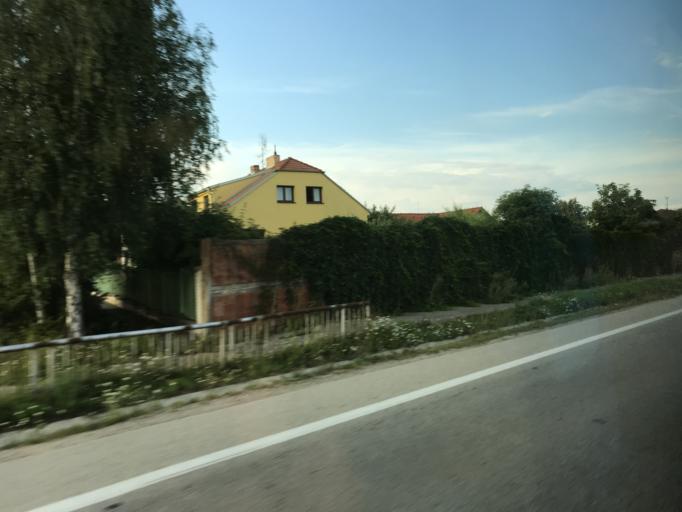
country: CZ
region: Jihocesky
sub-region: Okres Jindrichuv Hradec
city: Trebon
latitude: 49.0073
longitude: 14.7528
